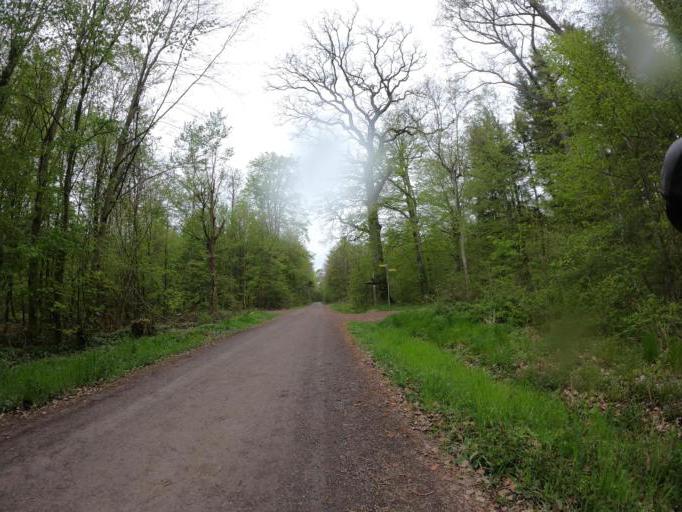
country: DE
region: Baden-Wuerttemberg
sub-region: Karlsruhe Region
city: Illingen
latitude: 48.9725
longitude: 8.9018
